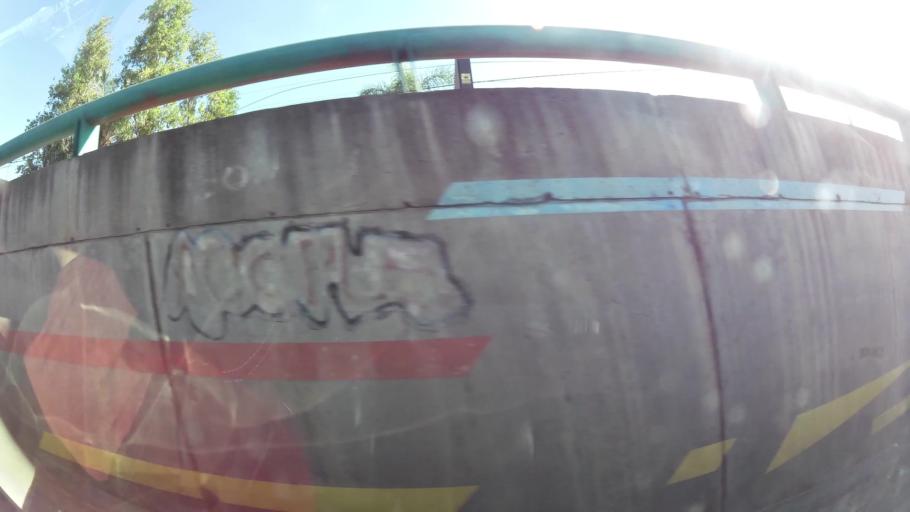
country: AR
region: Cordoba
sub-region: Departamento de Capital
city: Cordoba
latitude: -31.3590
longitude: -64.2395
